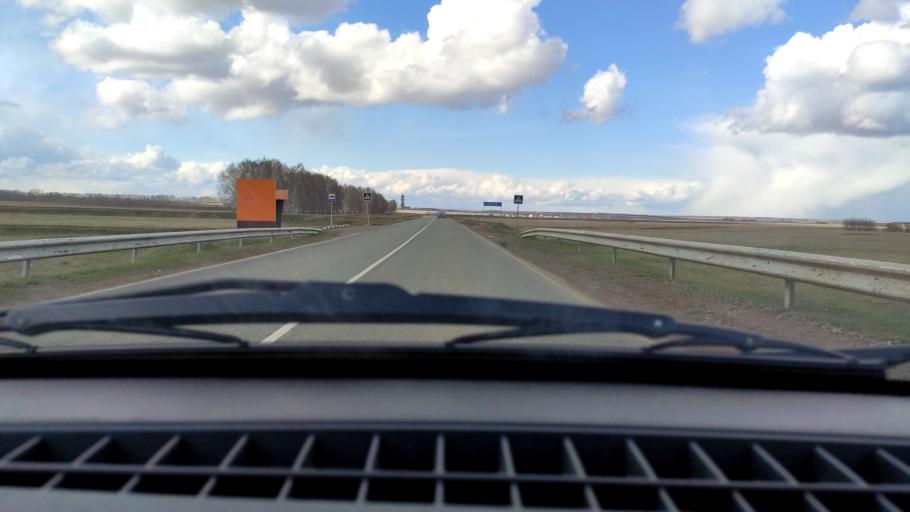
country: RU
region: Bashkortostan
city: Alekseyevka
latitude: 55.0809
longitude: 55.0665
